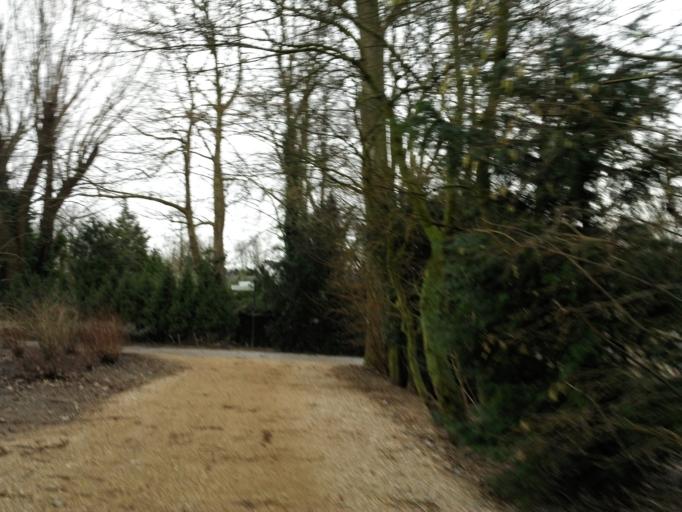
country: NL
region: North Holland
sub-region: Gemeente Amsterdam
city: Amsterdam
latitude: 52.3349
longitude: 4.8983
